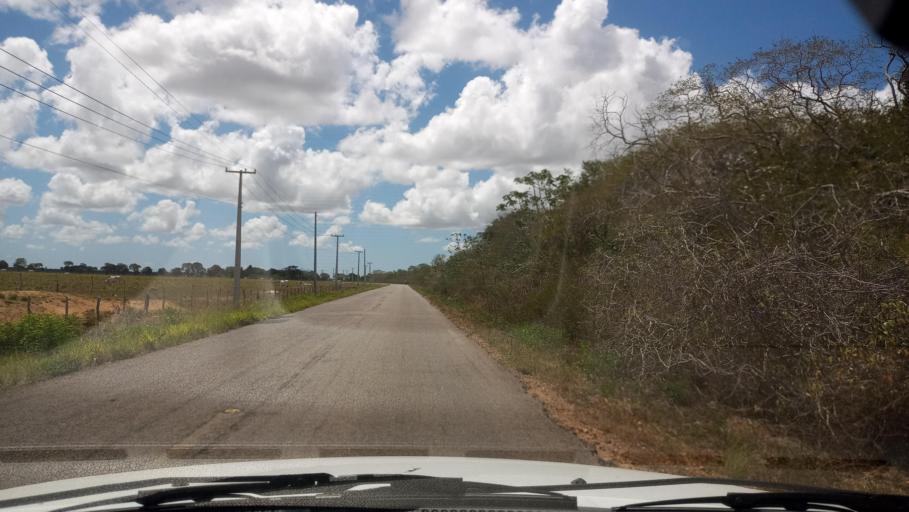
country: BR
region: Rio Grande do Norte
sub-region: Brejinho
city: Brejinho
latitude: -6.0416
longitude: -35.4115
